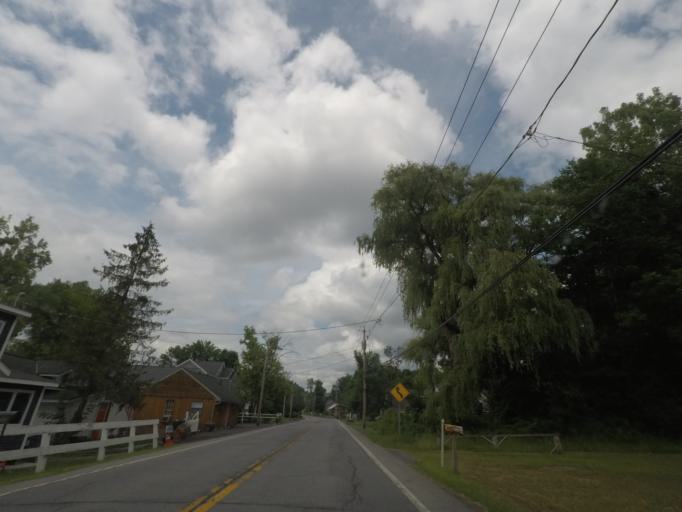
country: US
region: New York
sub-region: Saratoga County
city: Saratoga Springs
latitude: 42.9977
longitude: -73.7354
